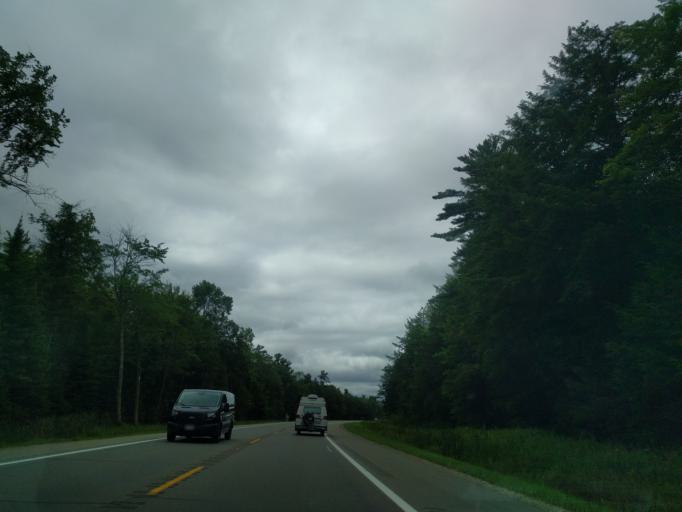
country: US
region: Michigan
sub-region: Menominee County
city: Menominee
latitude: 45.2948
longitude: -87.4411
